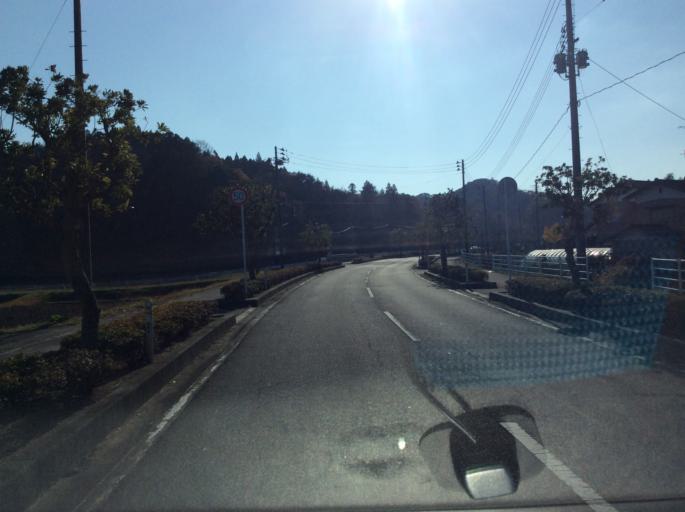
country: JP
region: Fukushima
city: Iwaki
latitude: 37.0301
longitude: 140.9350
